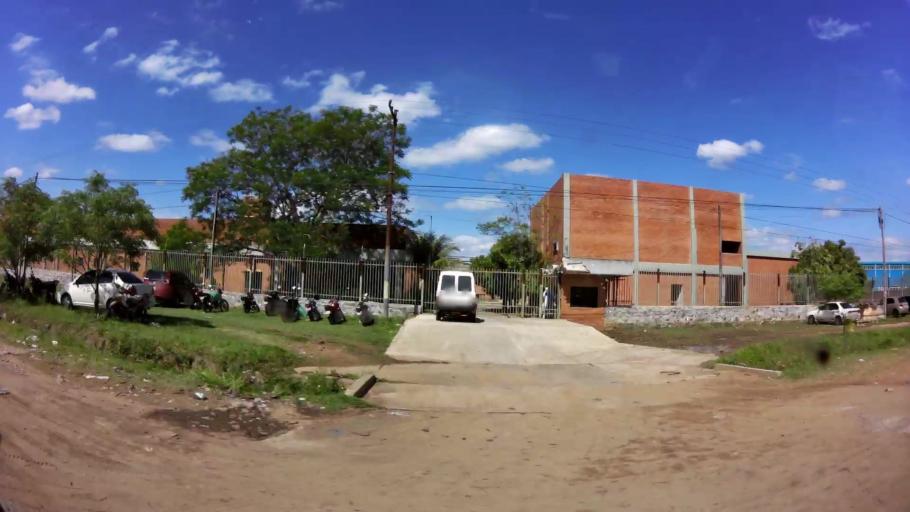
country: PY
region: Central
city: Fernando de la Mora
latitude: -25.2703
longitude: -57.5228
